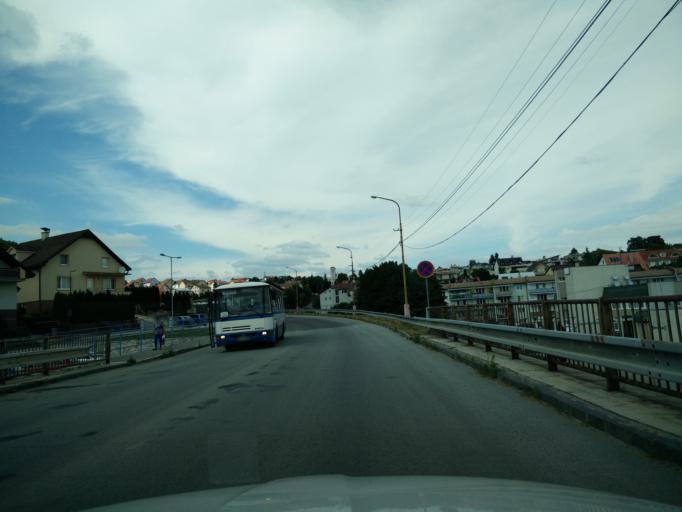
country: SK
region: Nitriansky
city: Bojnice
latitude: 48.8128
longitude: 18.5819
